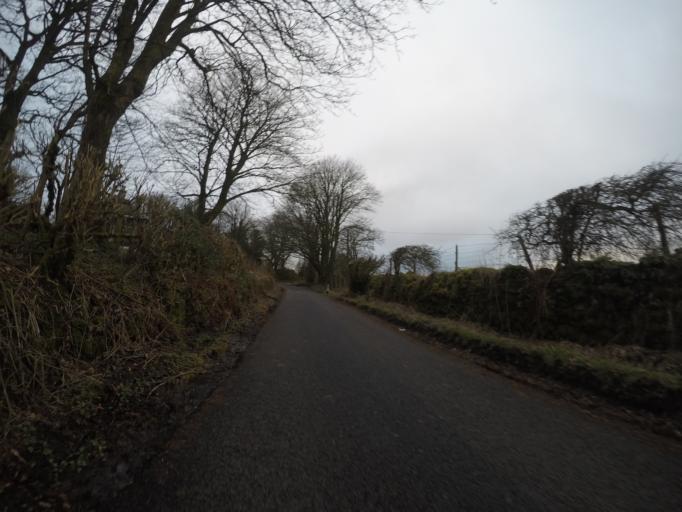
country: GB
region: Scotland
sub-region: North Ayrshire
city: Dalry
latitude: 55.7147
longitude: -4.7563
